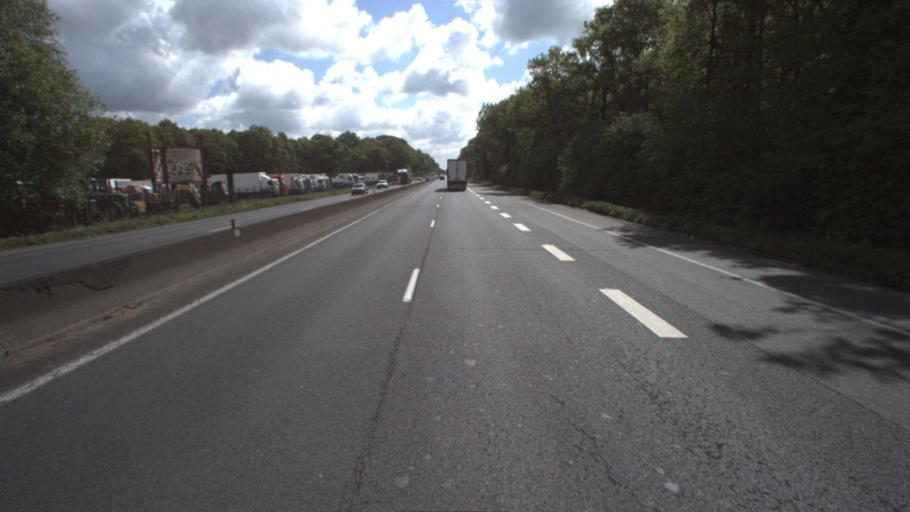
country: FR
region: Ile-de-France
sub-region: Departement de Seine-et-Marne
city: Pontault-Combault
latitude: 48.7728
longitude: 2.6178
